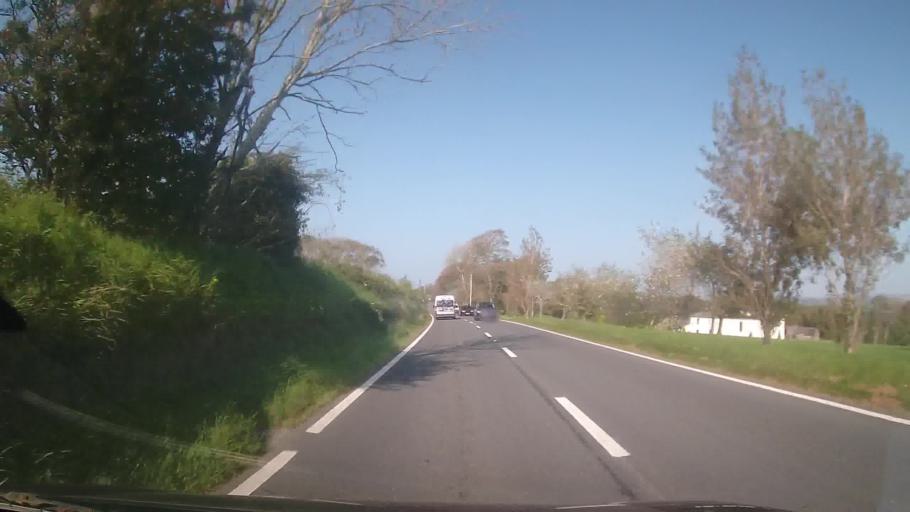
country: GB
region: Wales
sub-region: County of Ceredigion
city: Cardigan
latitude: 52.0611
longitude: -4.6831
